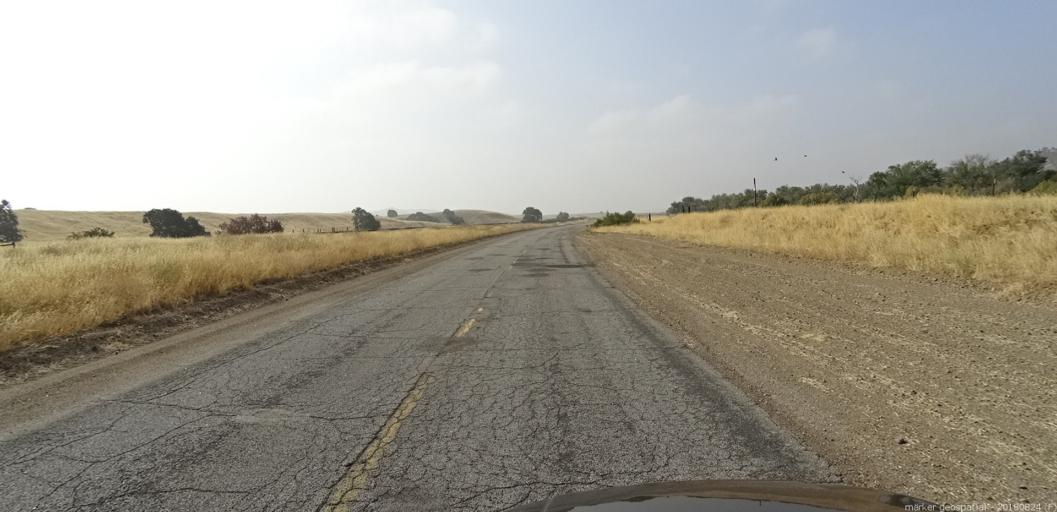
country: US
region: California
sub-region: San Luis Obispo County
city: San Miguel
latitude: 35.8471
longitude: -120.7537
